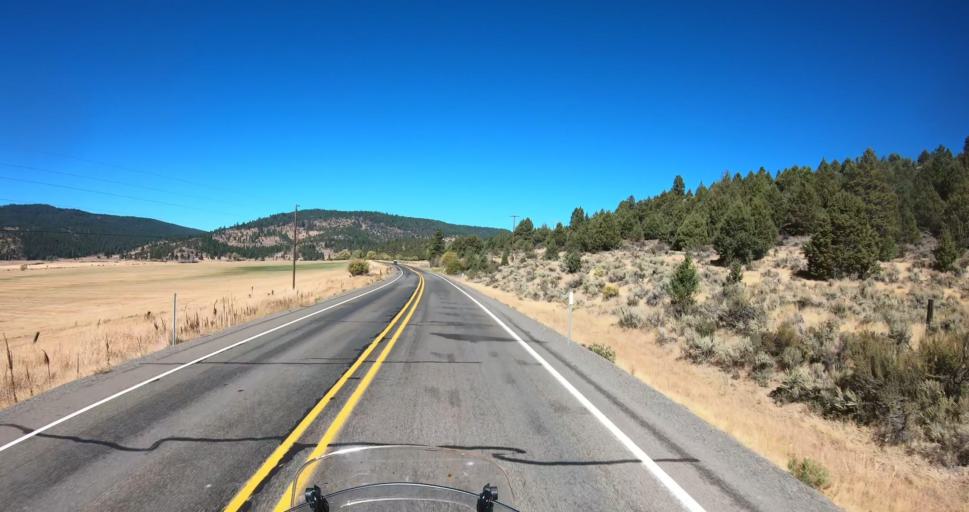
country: US
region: Oregon
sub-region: Lake County
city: Lakeview
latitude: 42.3749
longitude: -120.2983
